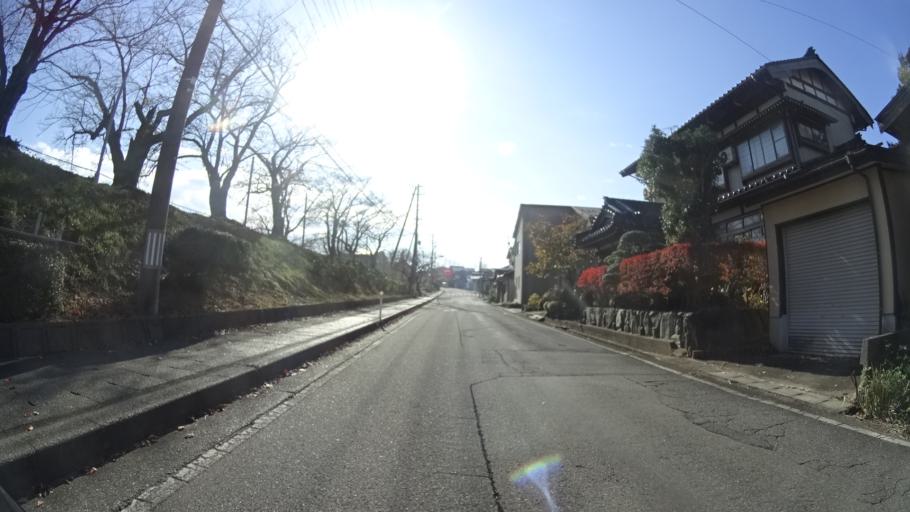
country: JP
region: Niigata
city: Itoigawa
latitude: 37.0332
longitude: 137.8583
